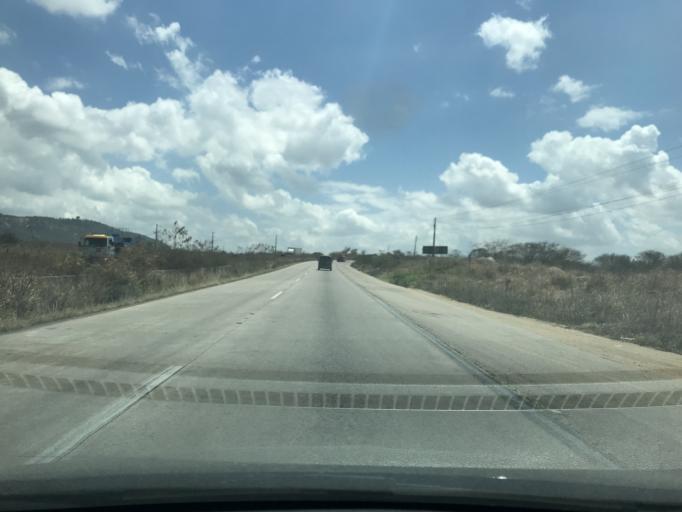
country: BR
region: Pernambuco
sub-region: Bezerros
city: Bezerros
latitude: -8.2951
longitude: -35.8273
